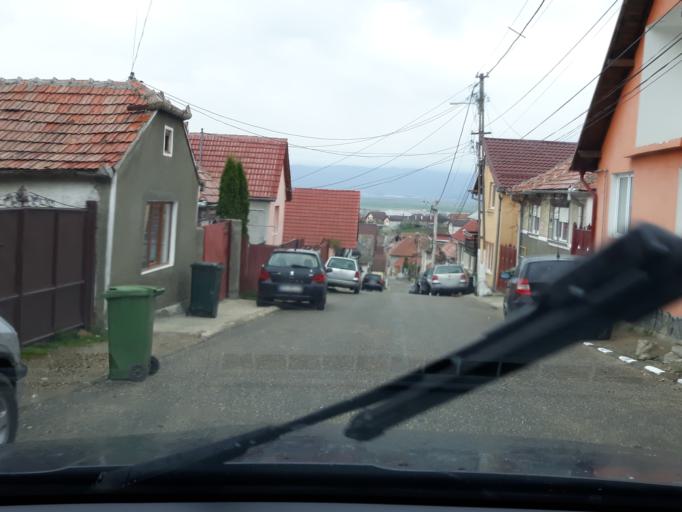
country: RO
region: Brasov
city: Codlea
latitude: 45.6974
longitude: 25.4328
